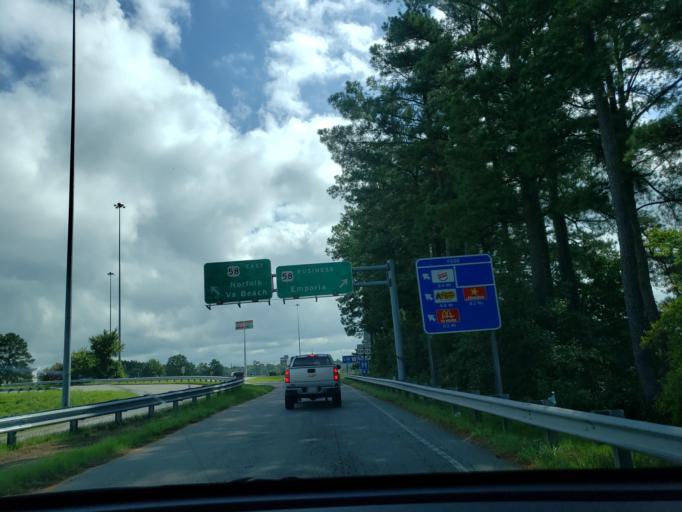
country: US
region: Virginia
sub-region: City of Emporia
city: Emporia
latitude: 36.7013
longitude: -77.5491
